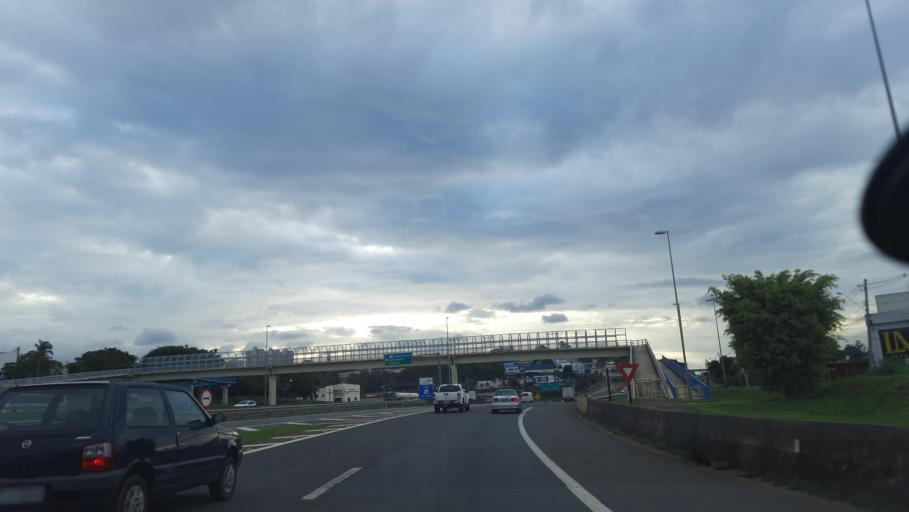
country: BR
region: Sao Paulo
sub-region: Campinas
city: Campinas
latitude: -22.8437
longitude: -47.0412
